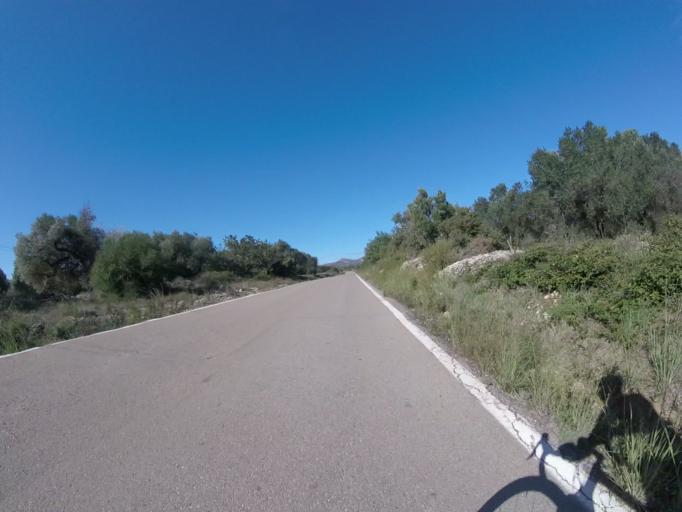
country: ES
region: Valencia
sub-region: Provincia de Castello
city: Chert/Xert
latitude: 40.4566
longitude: 0.1474
